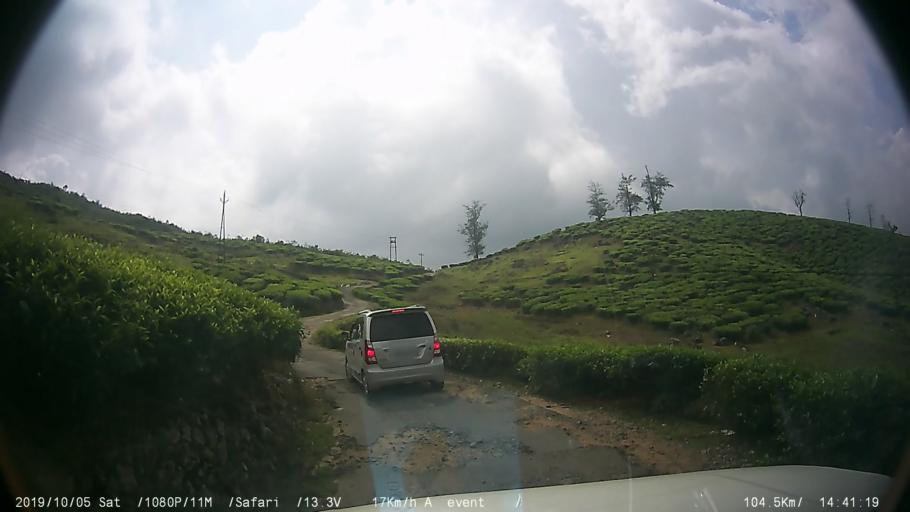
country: IN
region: Kerala
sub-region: Kottayam
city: Erattupetta
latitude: 9.6202
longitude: 76.9506
